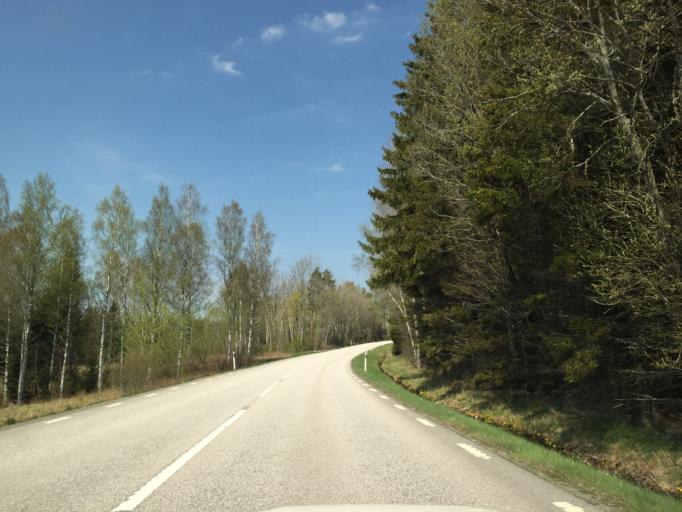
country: SE
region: Vaestra Goetaland
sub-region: Bengtsfors Kommun
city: Dals Langed
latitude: 58.9025
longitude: 12.2183
